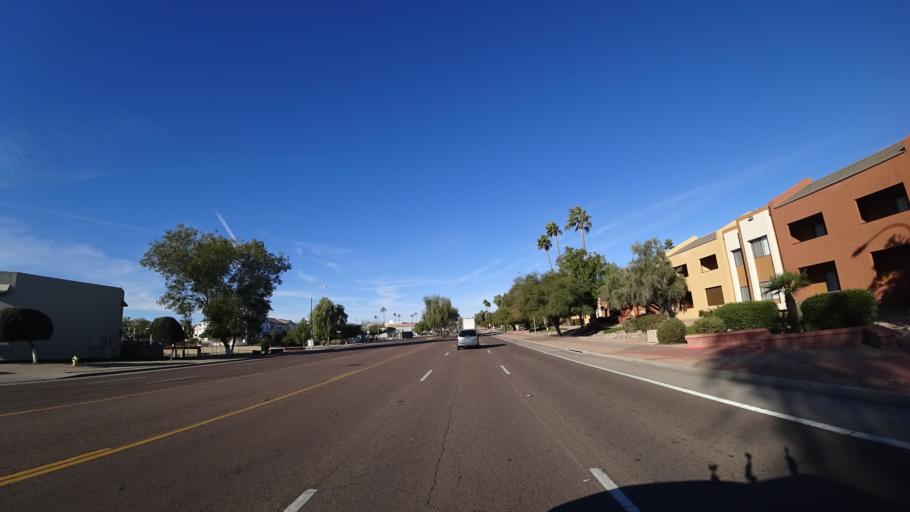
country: US
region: Arizona
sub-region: Maricopa County
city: Scottsdale
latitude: 33.4659
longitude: -111.8968
